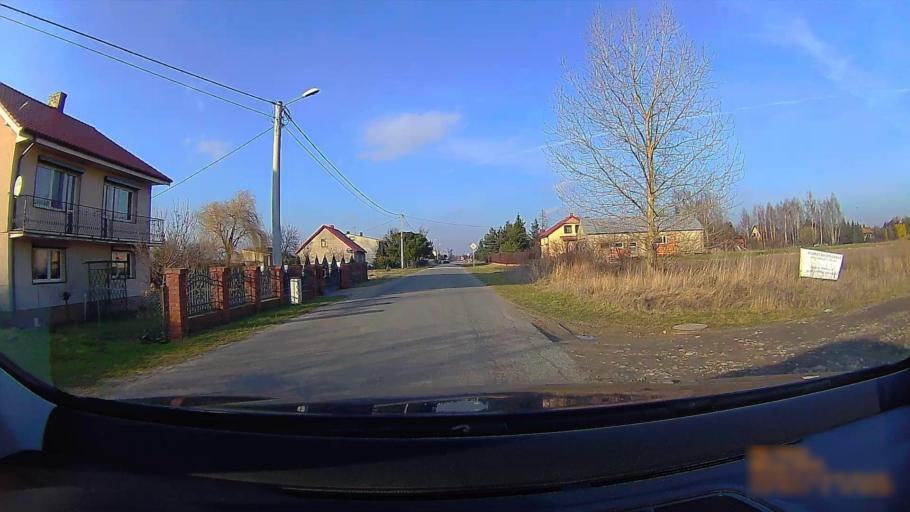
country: PL
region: Greater Poland Voivodeship
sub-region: Konin
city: Konin
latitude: 52.1812
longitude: 18.3010
